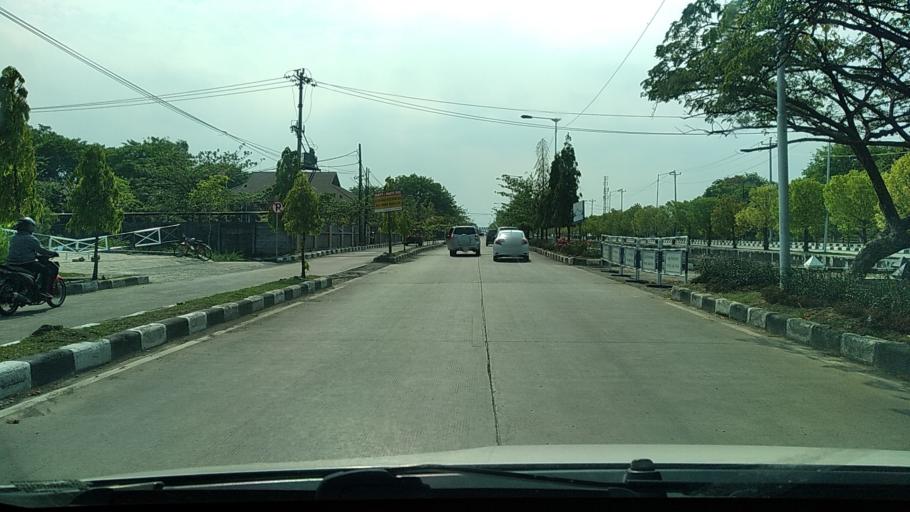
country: ID
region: Central Java
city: Semarang
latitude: -6.9627
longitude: 110.3898
